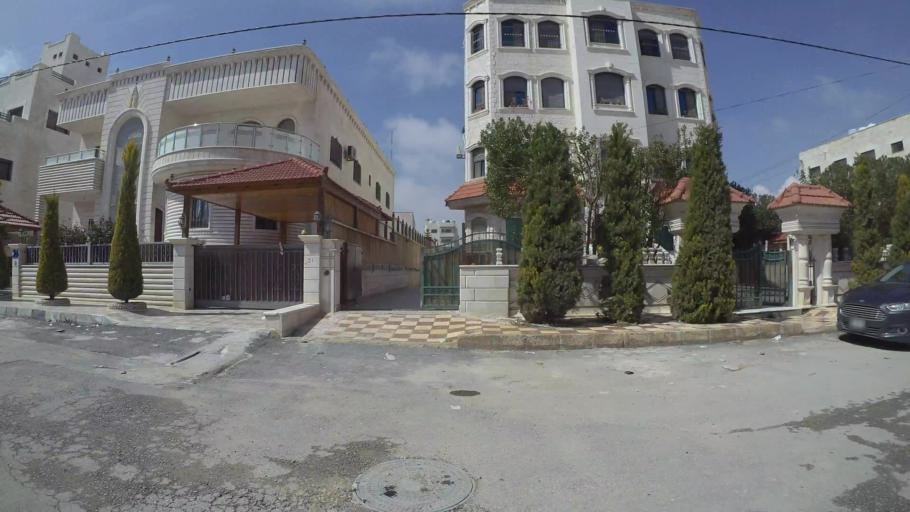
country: JO
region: Amman
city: Al Bunayyat ash Shamaliyah
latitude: 31.9010
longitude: 35.8905
